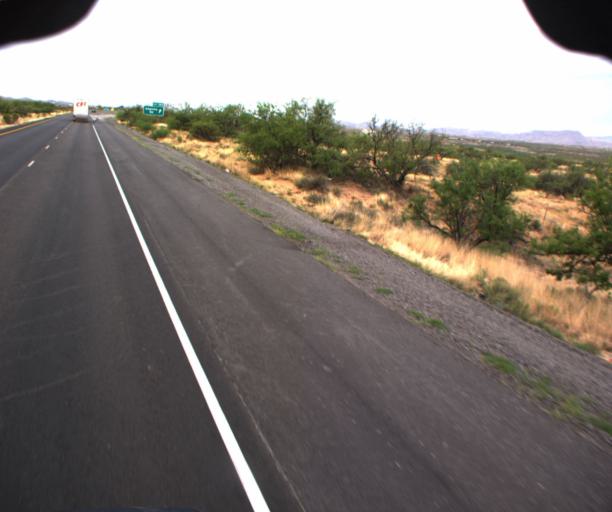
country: US
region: Arizona
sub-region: Cochise County
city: Mescal
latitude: 31.9753
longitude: -110.5044
